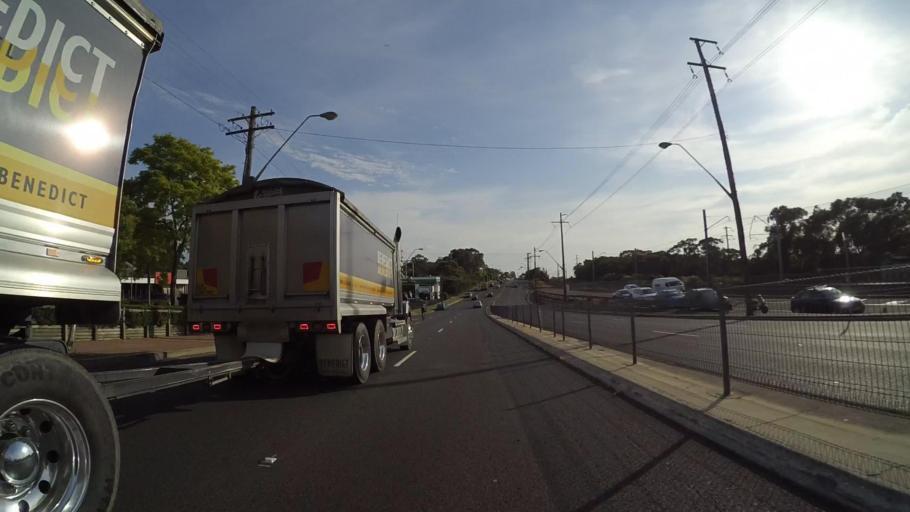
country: AU
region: New South Wales
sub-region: Sutherland Shire
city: Engadine
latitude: -34.0669
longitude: 151.0151
